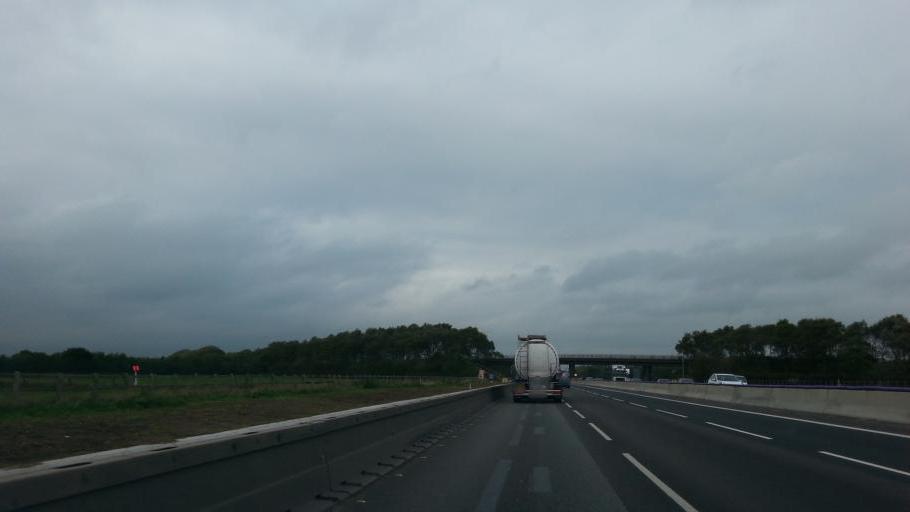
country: GB
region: England
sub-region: Cheshire East
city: Holmes Chapel
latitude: 53.2250
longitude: -2.3935
